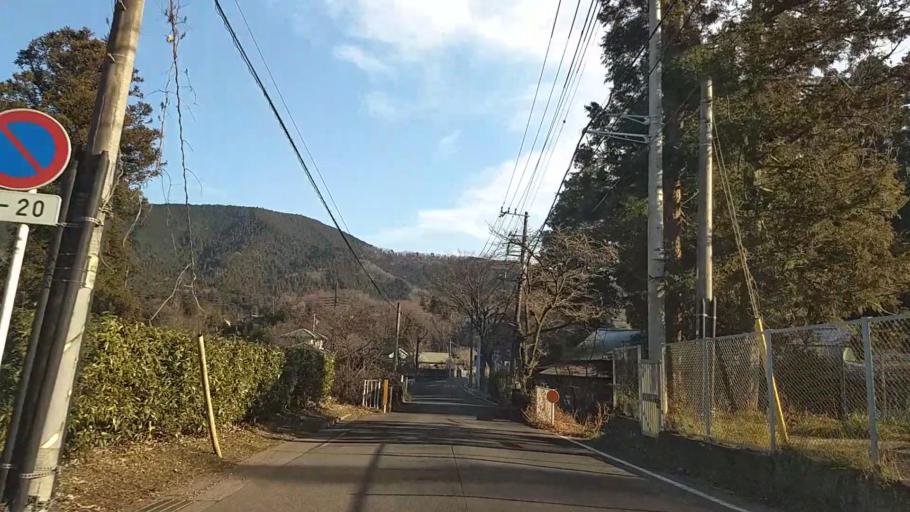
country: JP
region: Yamanashi
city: Uenohara
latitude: 35.5482
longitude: 139.2185
